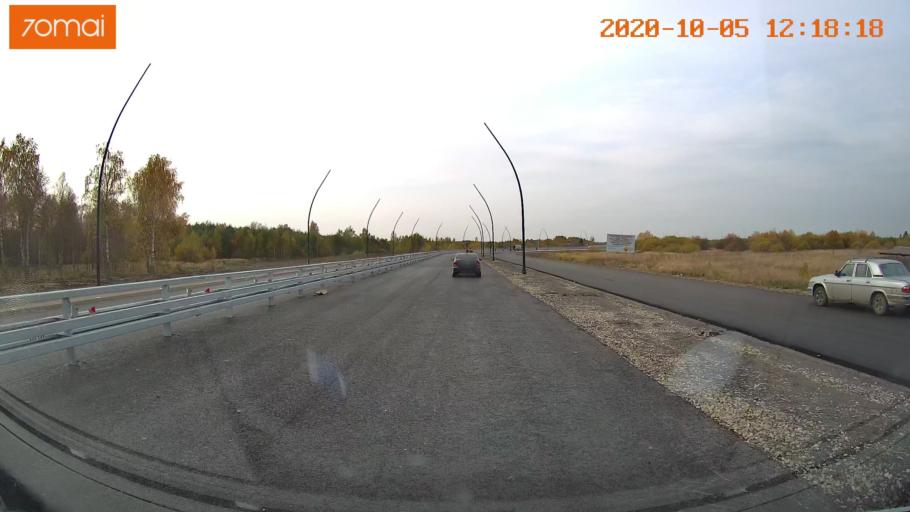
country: RU
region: Ivanovo
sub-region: Gorod Ivanovo
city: Ivanovo
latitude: 56.9523
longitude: 40.9430
